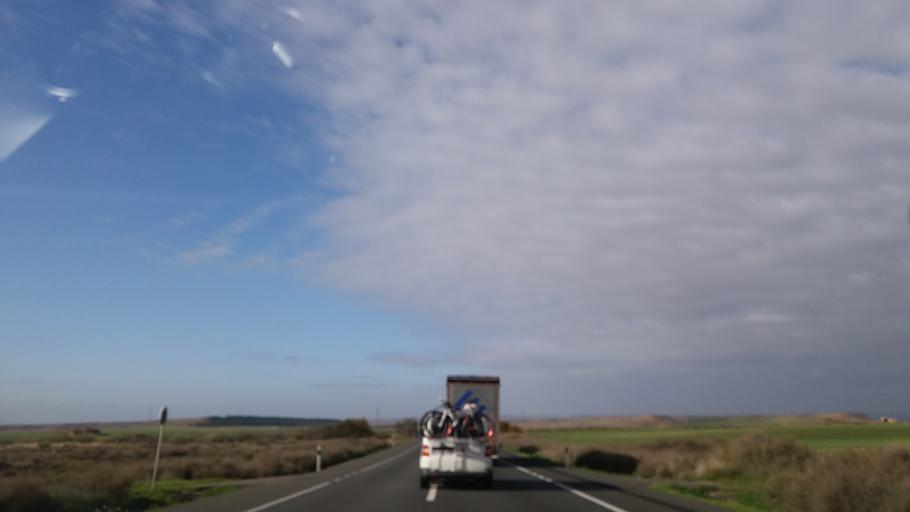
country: ES
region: Aragon
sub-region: Provincia de Huesca
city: Saidi / Zaidin
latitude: 41.5186
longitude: 0.2217
